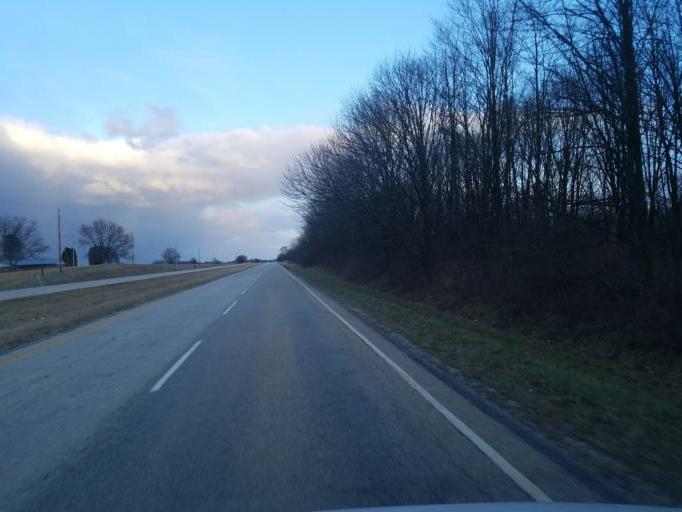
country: US
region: Indiana
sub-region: Henry County
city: Knightstown
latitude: 39.8021
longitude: -85.4686
